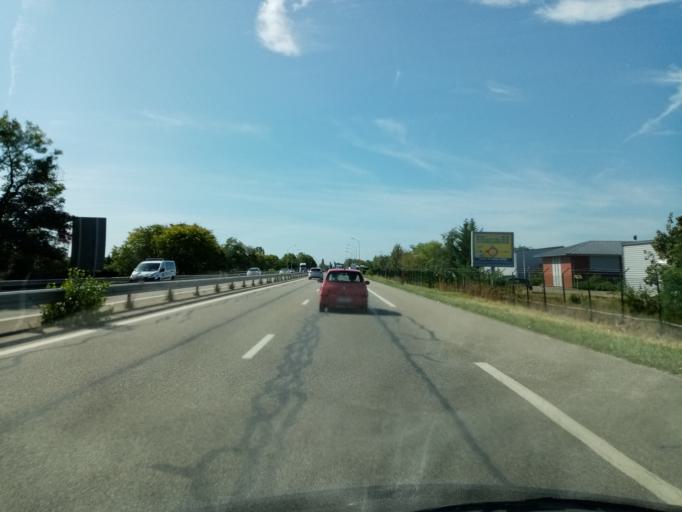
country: FR
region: Alsace
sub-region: Departement du Haut-Rhin
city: Houssen
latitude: 48.1135
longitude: 7.3641
